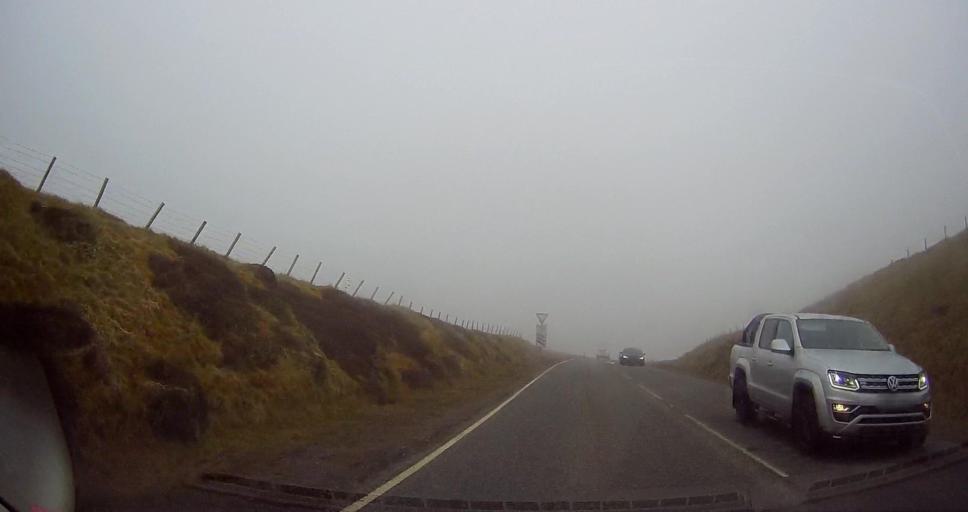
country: GB
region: Scotland
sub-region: Shetland Islands
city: Lerwick
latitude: 60.1390
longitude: -1.2192
